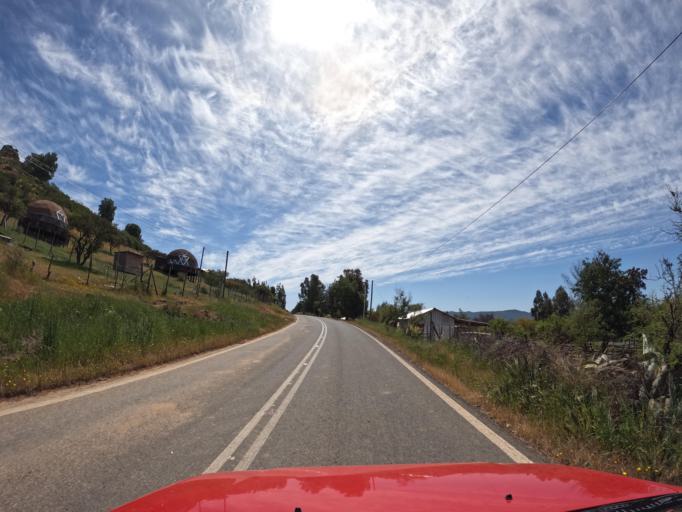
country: CL
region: Maule
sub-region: Provincia de Talca
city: Talca
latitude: -35.0411
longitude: -71.7529
